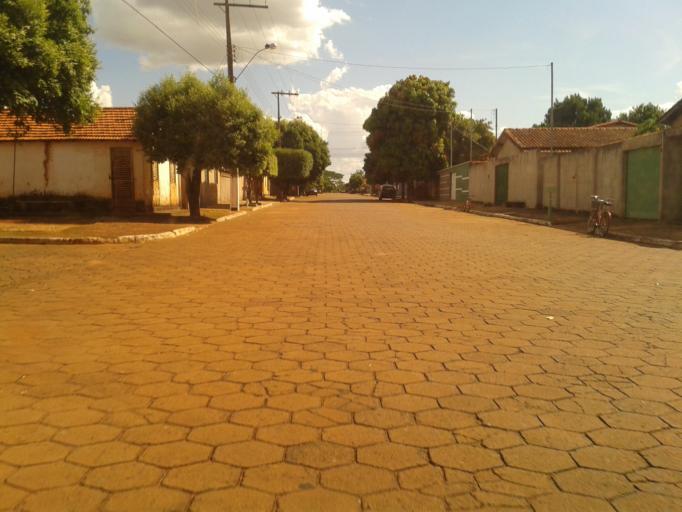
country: BR
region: Minas Gerais
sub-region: Santa Vitoria
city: Santa Vitoria
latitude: -18.6954
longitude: -49.9445
